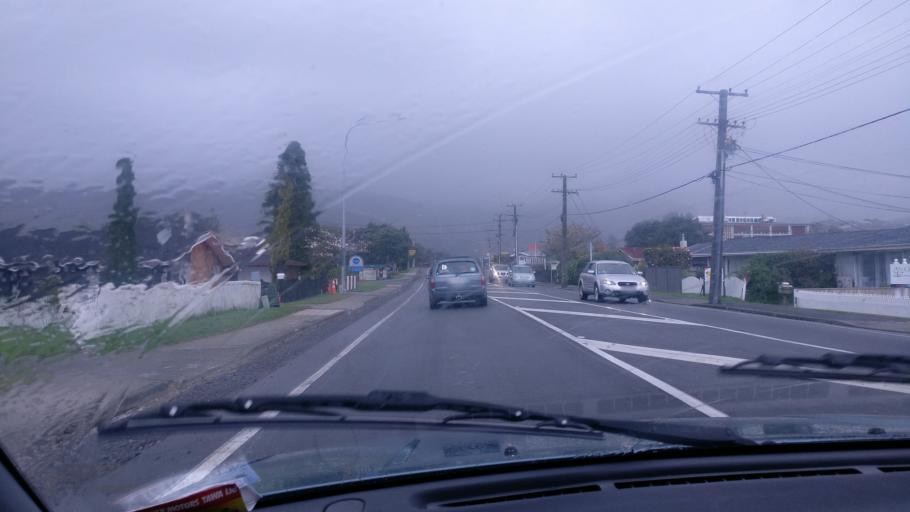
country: NZ
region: Wellington
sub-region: Kapiti Coast District
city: Paraparaumu
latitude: -40.9118
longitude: 175.0031
